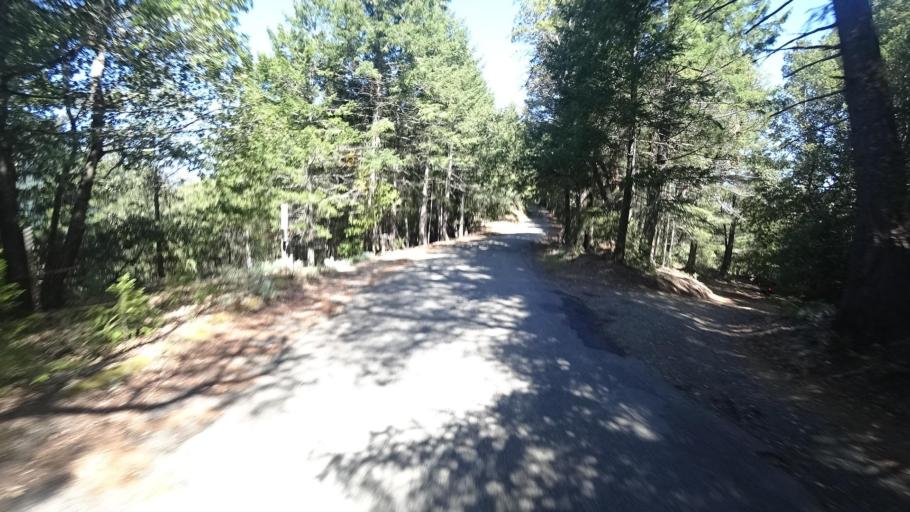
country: US
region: California
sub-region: Humboldt County
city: Redway
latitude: 40.1657
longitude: -124.0830
